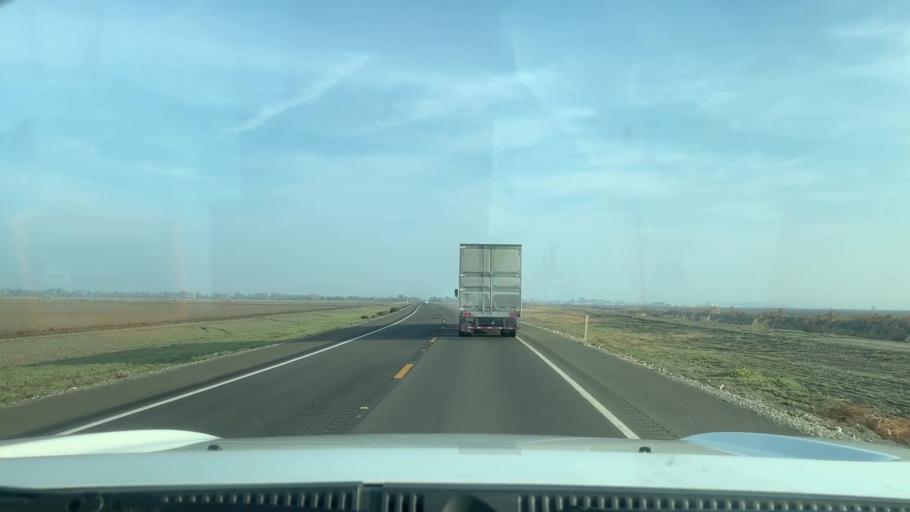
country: US
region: California
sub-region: Kings County
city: Stratford
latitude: 36.1685
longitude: -119.8433
